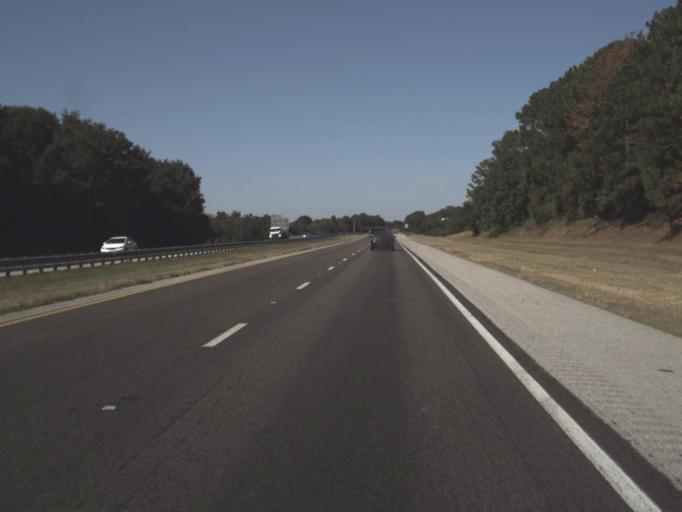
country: US
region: Florida
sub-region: Orange County
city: Oakland
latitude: 28.5575
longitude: -81.6731
